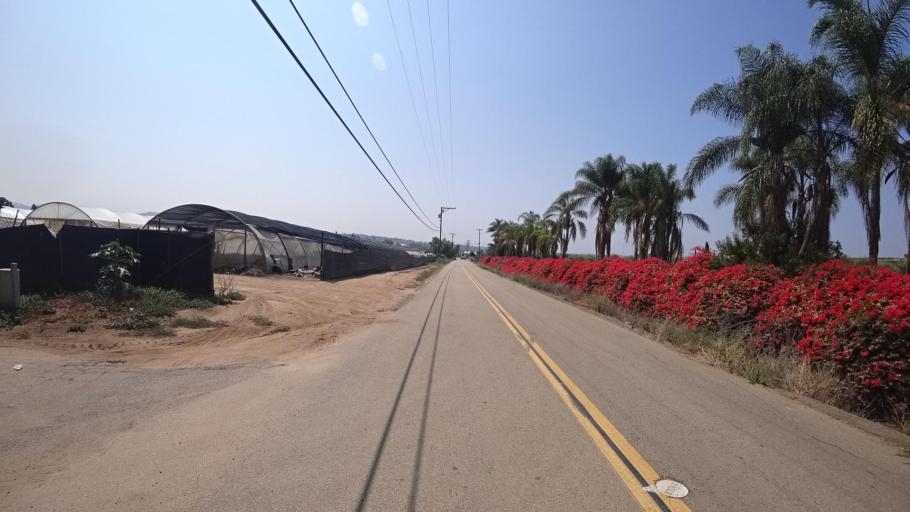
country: US
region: California
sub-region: San Diego County
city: Bonsall
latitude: 33.2722
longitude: -117.2449
